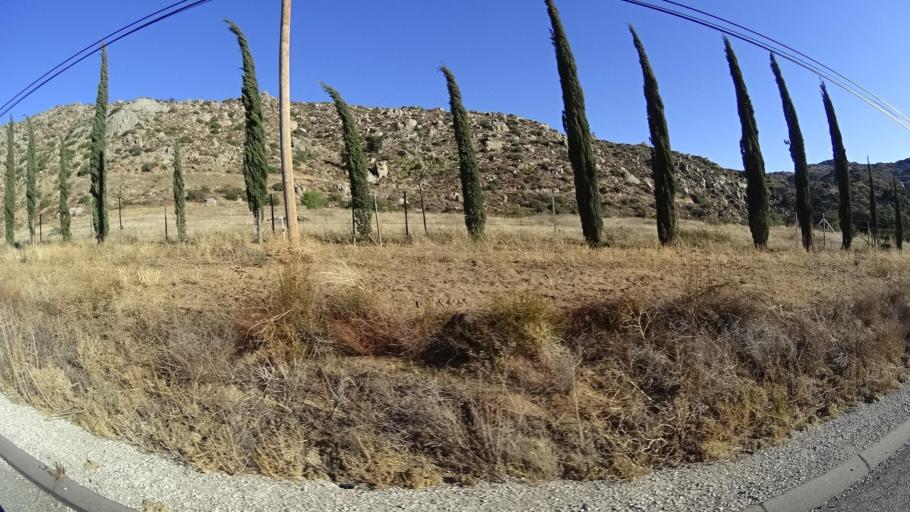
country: MX
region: Baja California
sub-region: Tecate
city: Hacienda Tecate
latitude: 32.5974
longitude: -116.5575
